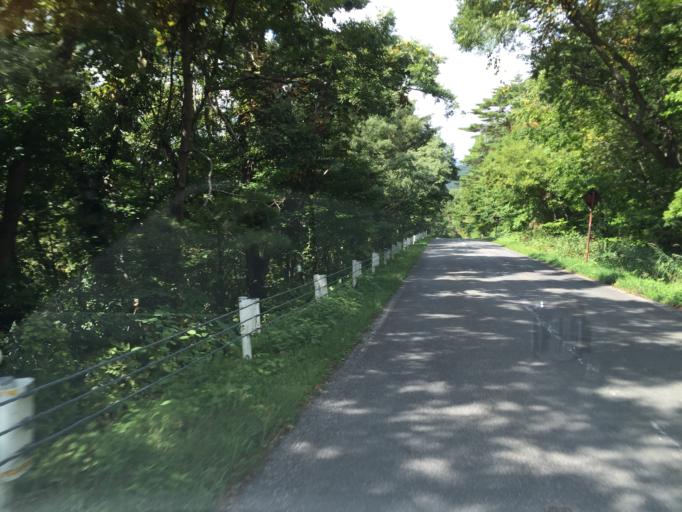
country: JP
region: Fukushima
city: Inawashiro
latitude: 37.6351
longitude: 140.0521
